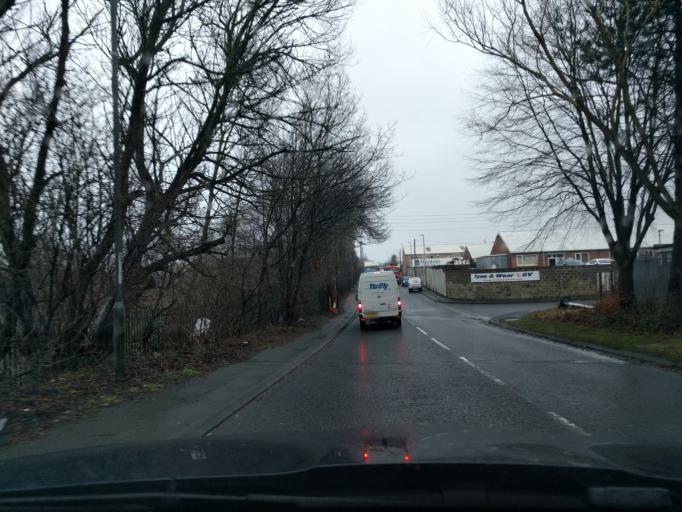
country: GB
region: England
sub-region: Gateshead
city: Felling
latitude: 54.9554
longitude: -1.5639
